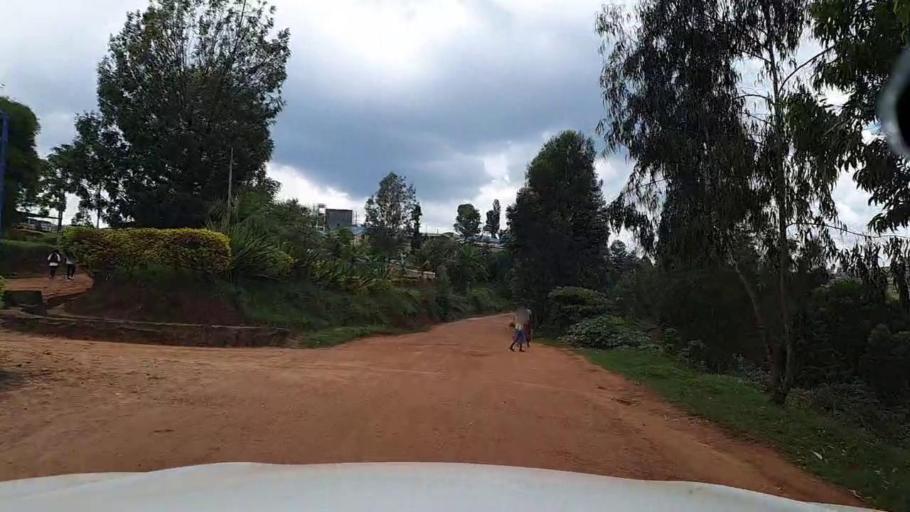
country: BI
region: Kayanza
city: Kayanza
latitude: -2.7134
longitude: 29.5368
